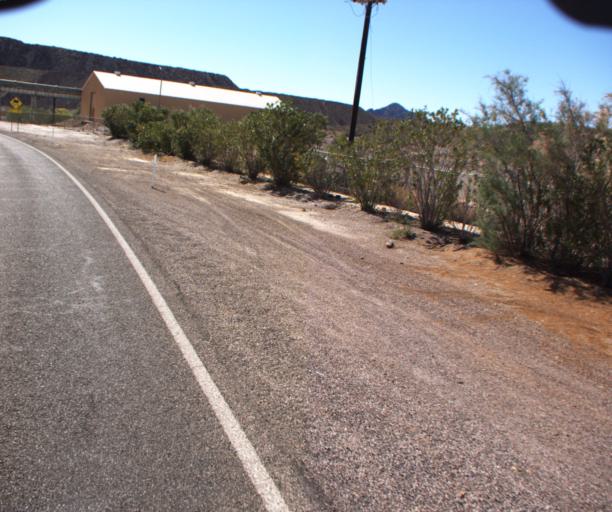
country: US
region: Arizona
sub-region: Pima County
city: Ajo
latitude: 32.3699
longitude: -112.8538
